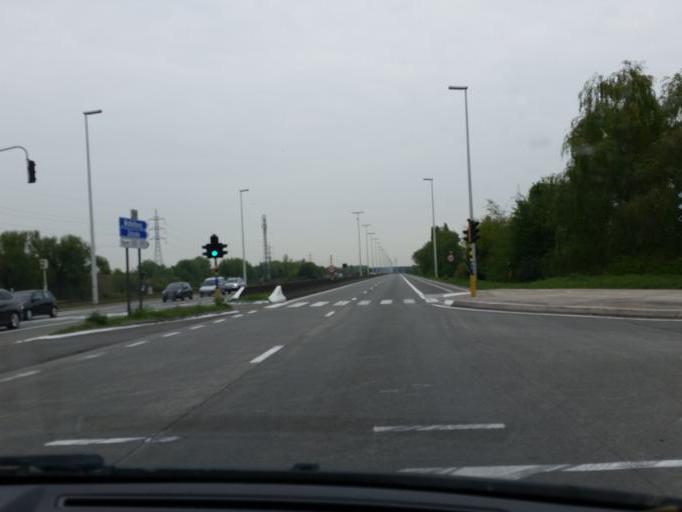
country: BE
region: Flanders
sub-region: Provincie Oost-Vlaanderen
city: Zelzate
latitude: 51.1567
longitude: 3.8143
